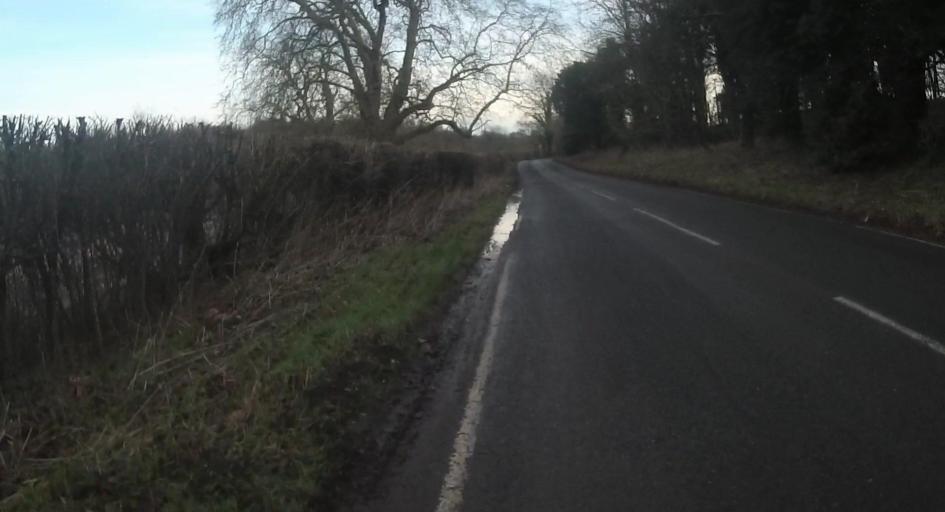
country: GB
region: England
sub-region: Hampshire
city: Overton
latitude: 51.2216
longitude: -1.3764
